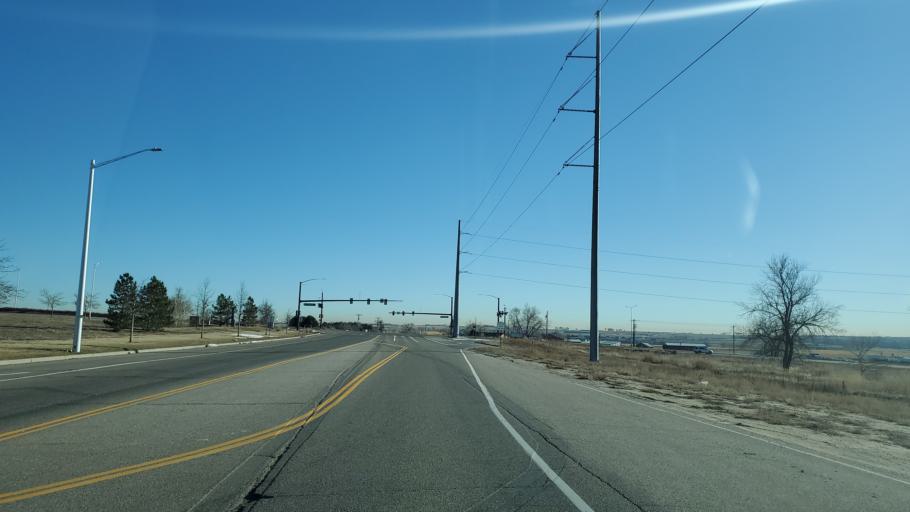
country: US
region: Colorado
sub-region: Boulder County
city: Erie
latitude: 39.9866
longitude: -104.9805
